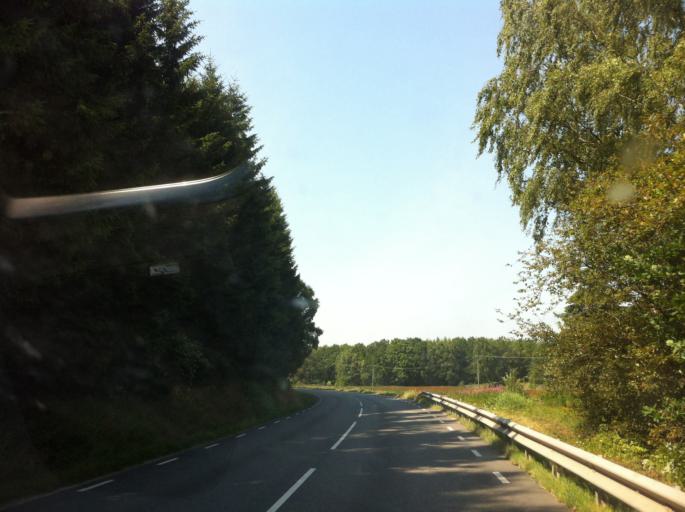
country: SE
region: Skane
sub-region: Hoors Kommun
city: Hoeoer
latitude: 56.0129
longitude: 13.5184
